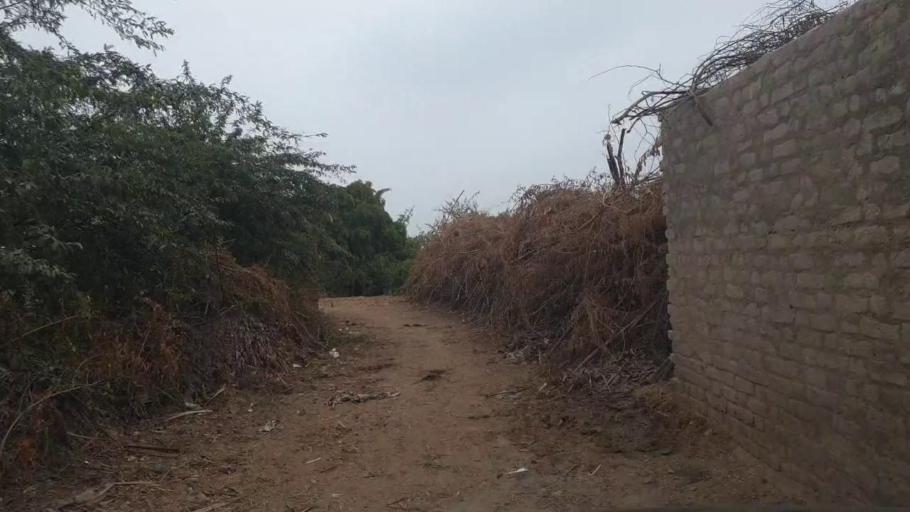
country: PK
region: Sindh
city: Tando Adam
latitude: 25.8318
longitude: 68.7146
